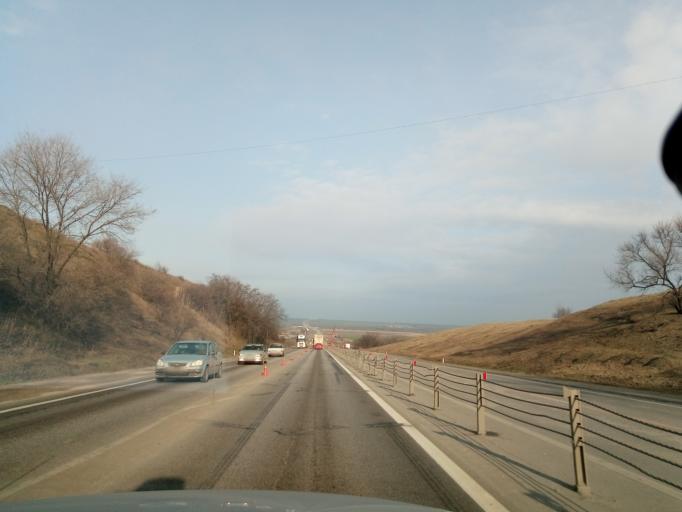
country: RU
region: Rostov
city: Grushevskaya
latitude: 47.4371
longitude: 39.9746
